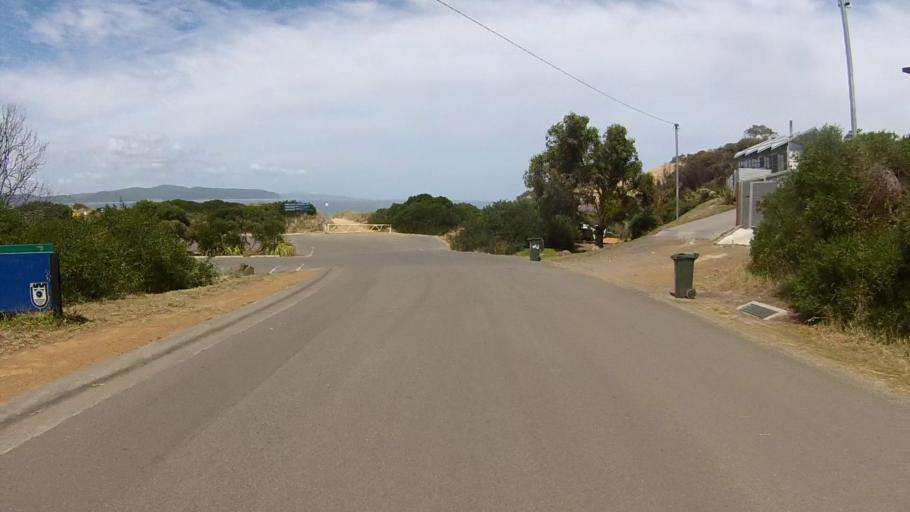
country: AU
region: Tasmania
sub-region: Clarence
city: Sandford
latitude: -42.9915
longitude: 147.5234
